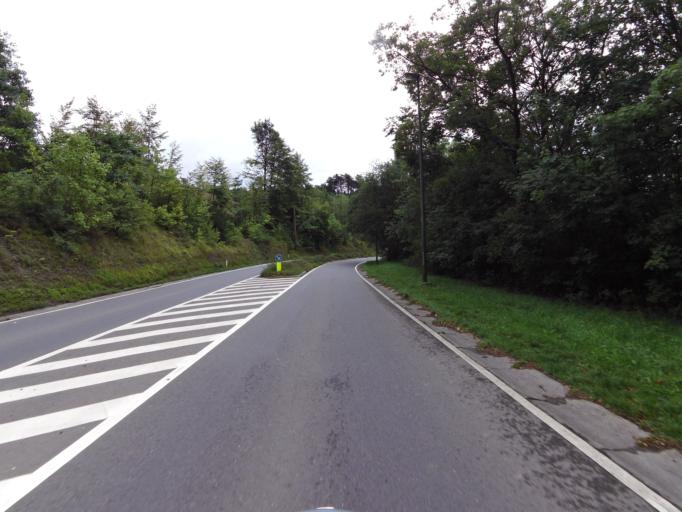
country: BE
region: Wallonia
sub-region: Province de Namur
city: Rochefort
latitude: 50.1300
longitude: 5.1895
